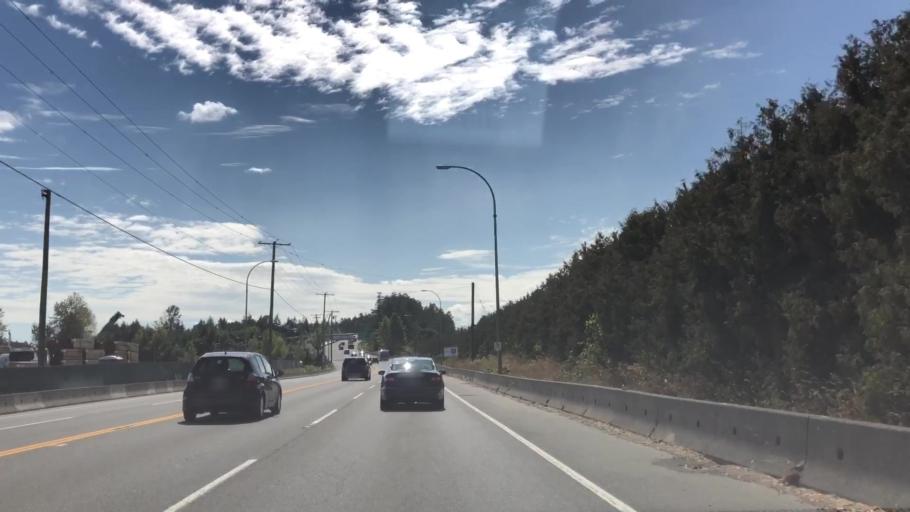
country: CA
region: British Columbia
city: Nanaimo
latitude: 49.1519
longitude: -123.8892
